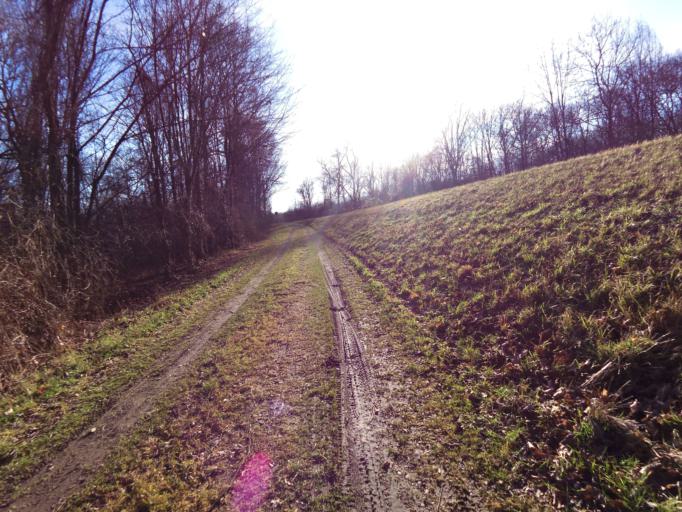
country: DE
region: Bavaria
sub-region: Upper Bavaria
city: Wang
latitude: 48.4854
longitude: 11.9563
